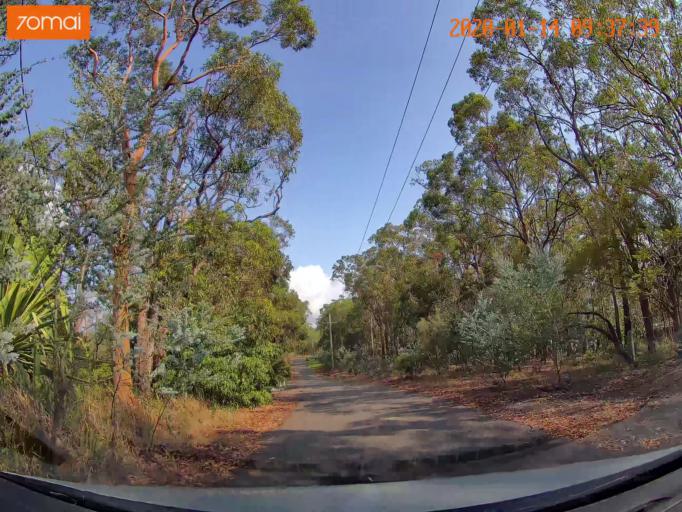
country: AU
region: New South Wales
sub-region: Wyong Shire
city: Kingfisher Shores
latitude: -33.1155
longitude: 151.5592
